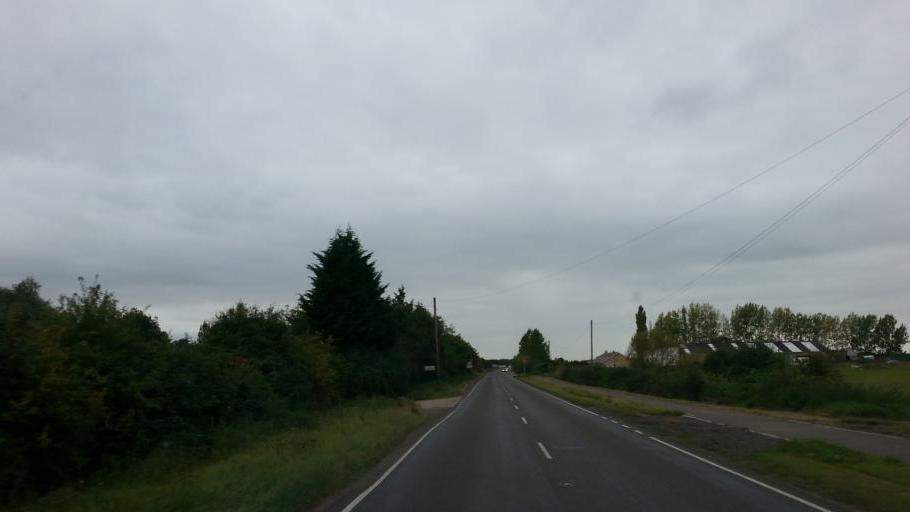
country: GB
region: England
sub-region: Cambridgeshire
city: Needingworth
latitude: 52.3416
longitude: -0.0123
